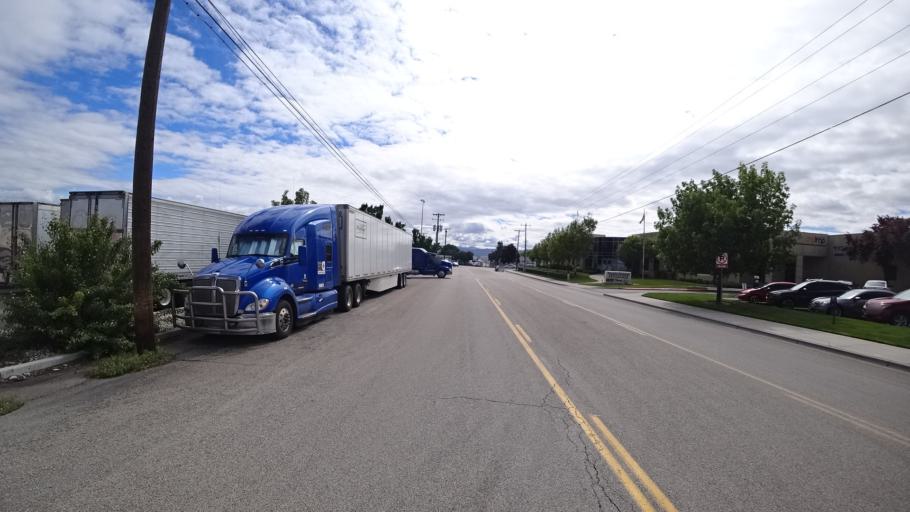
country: US
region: Idaho
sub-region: Ada County
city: Boise
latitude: 43.5643
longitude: -116.2003
